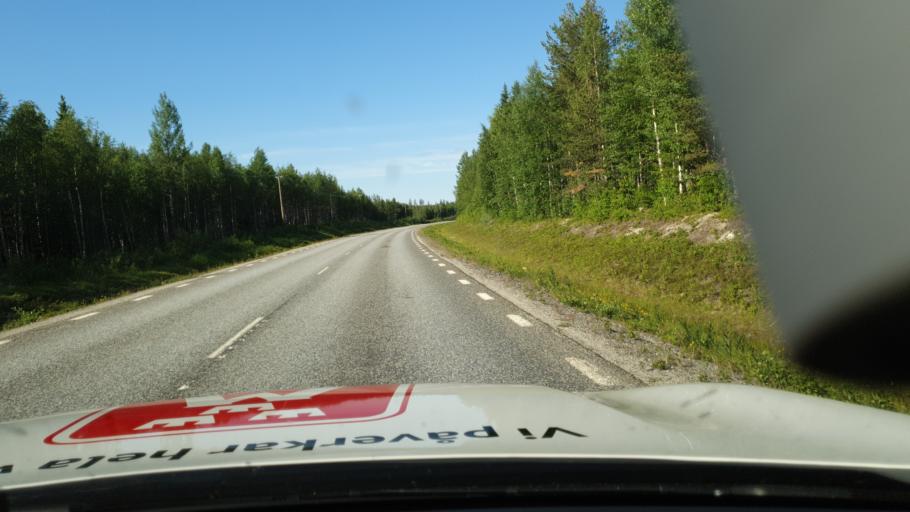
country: SE
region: Vaesterbotten
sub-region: Lycksele Kommun
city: Lycksele
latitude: 64.5391
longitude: 18.4971
